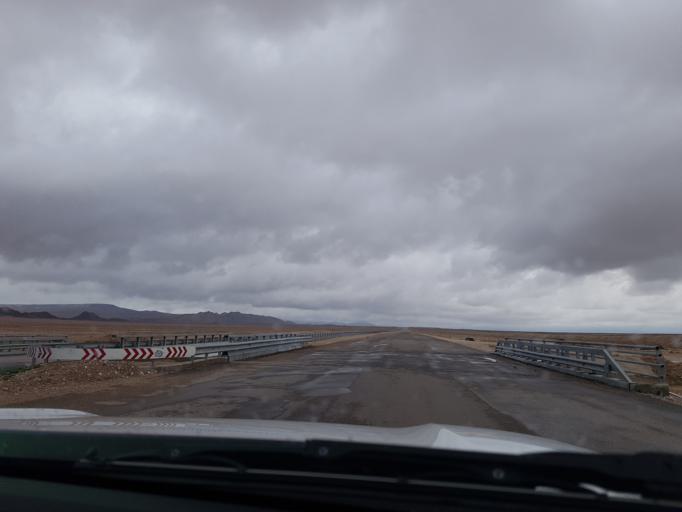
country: TM
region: Balkan
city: Balkanabat
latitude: 39.9114
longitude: 53.9095
